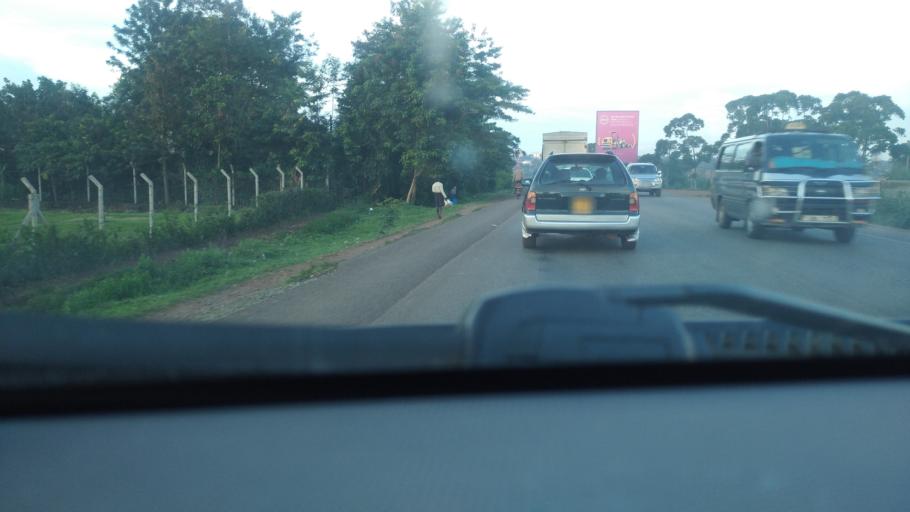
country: UG
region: Eastern Region
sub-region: Iganga District
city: Iganga
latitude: 0.6030
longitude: 33.4620
